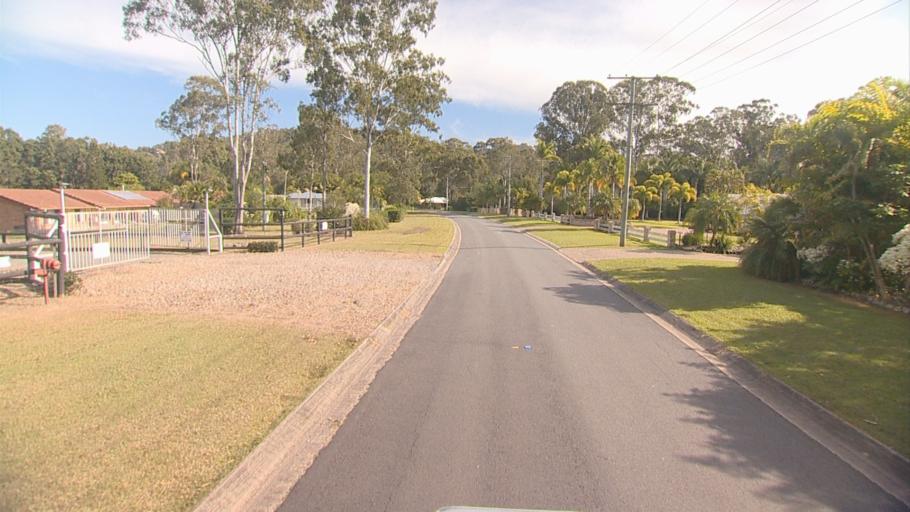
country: AU
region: Queensland
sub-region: Logan
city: Windaroo
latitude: -27.7632
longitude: 153.1924
